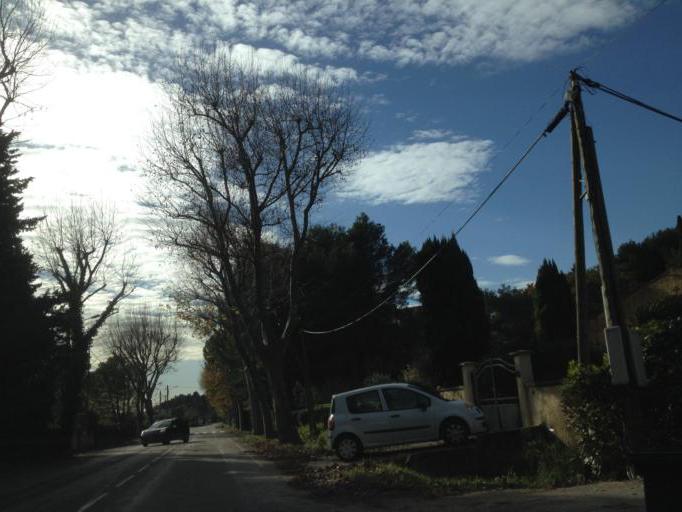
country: FR
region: Provence-Alpes-Cote d'Azur
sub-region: Departement du Vaucluse
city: Bedarrides
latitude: 44.0387
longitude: 4.8817
